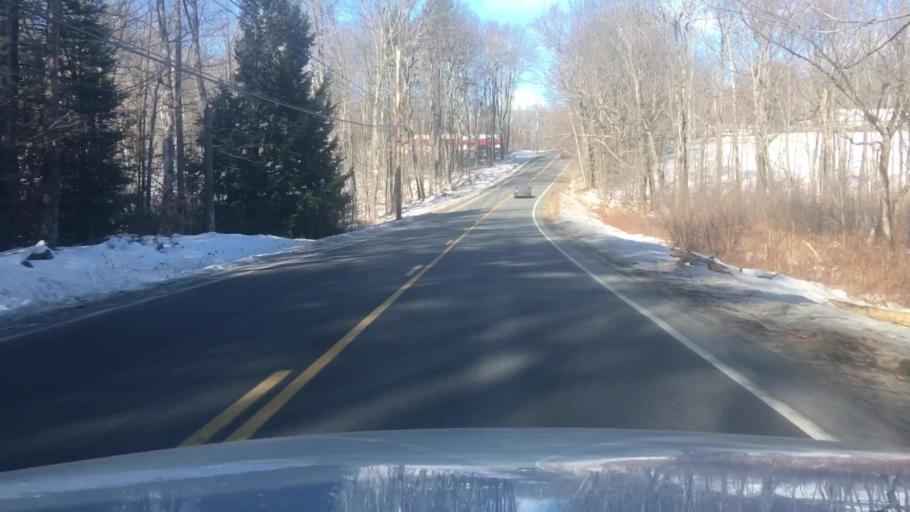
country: US
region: Maine
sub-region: Somerset County
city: Skowhegan
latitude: 44.7312
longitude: -69.6803
